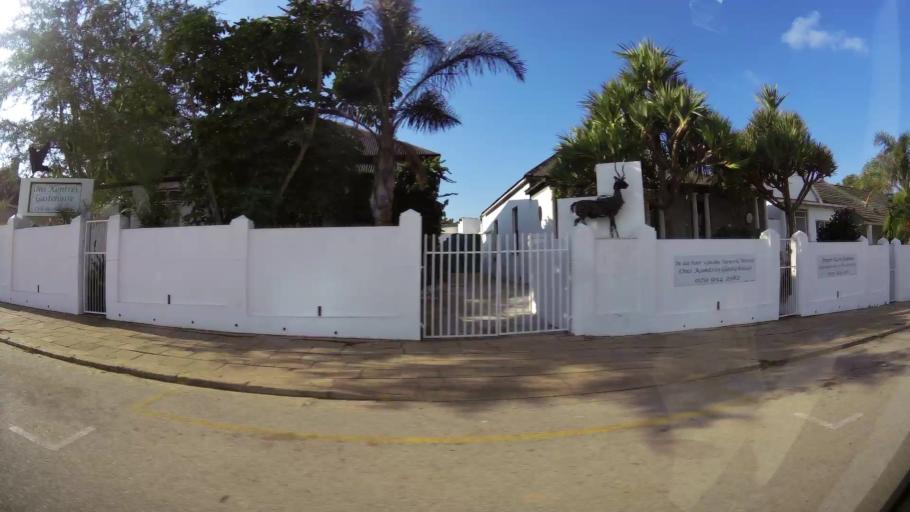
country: ZA
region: Eastern Cape
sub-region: Nelson Mandela Bay Metropolitan Municipality
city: Uitenhage
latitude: -33.7701
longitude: 25.4052
